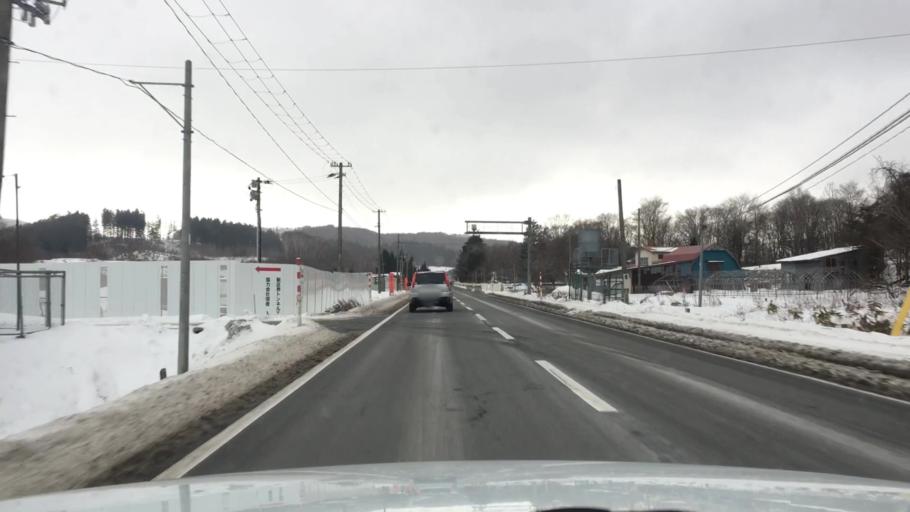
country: JP
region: Iwate
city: Morioka-shi
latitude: 39.6459
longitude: 141.3655
